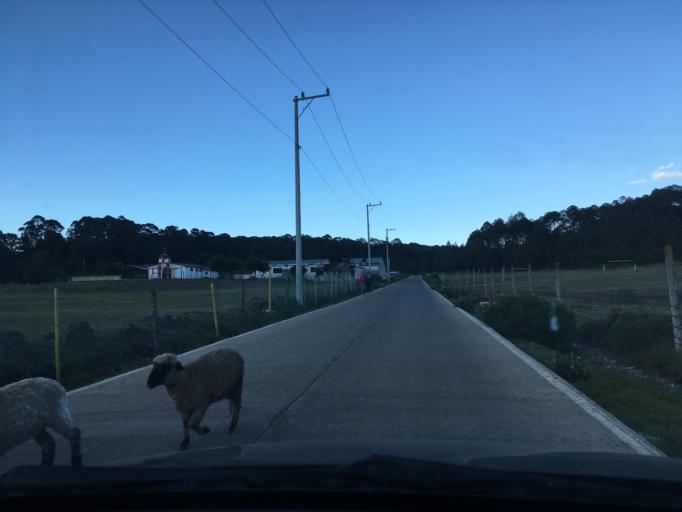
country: MX
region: Hidalgo
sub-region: Omitlan de Juarez
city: San Antonio el Paso
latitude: 20.1485
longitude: -98.6006
